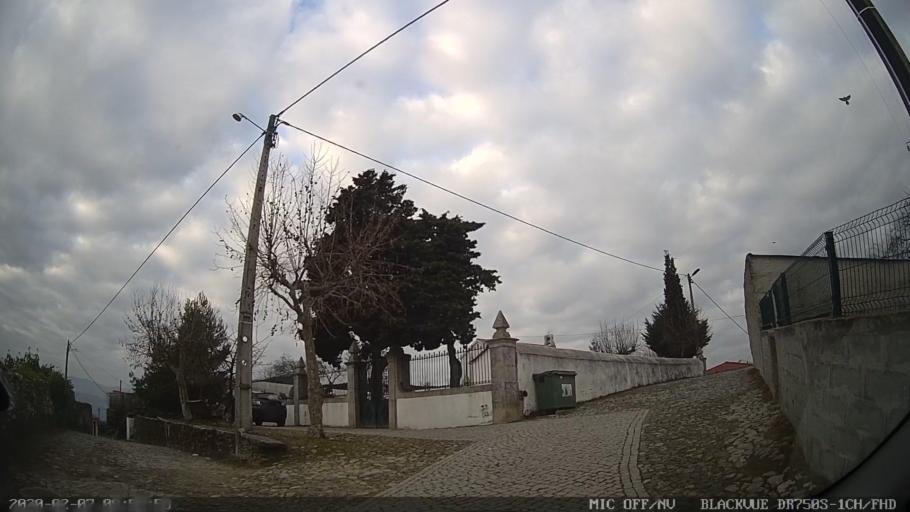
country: PT
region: Vila Real
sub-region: Sabrosa
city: Sabrosa
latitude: 41.2108
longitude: -7.5290
